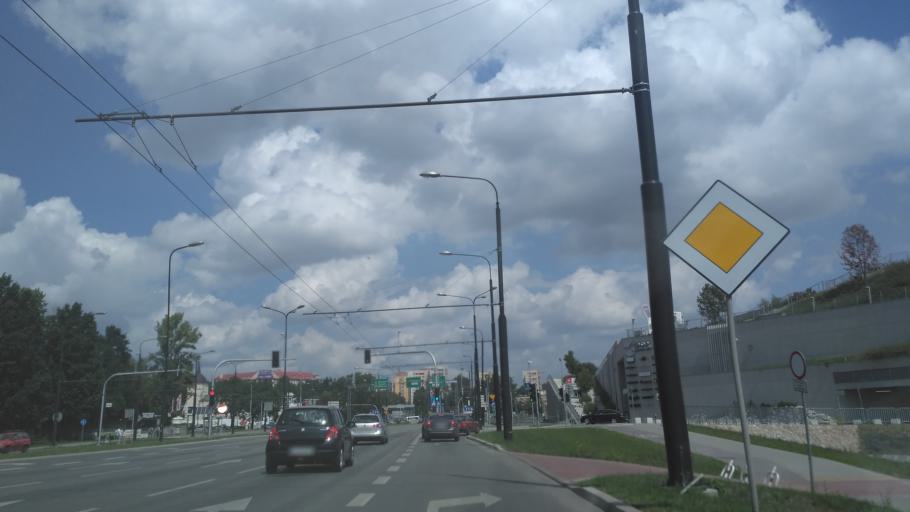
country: PL
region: Lublin Voivodeship
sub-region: Powiat lubelski
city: Lublin
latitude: 51.2485
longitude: 22.5746
